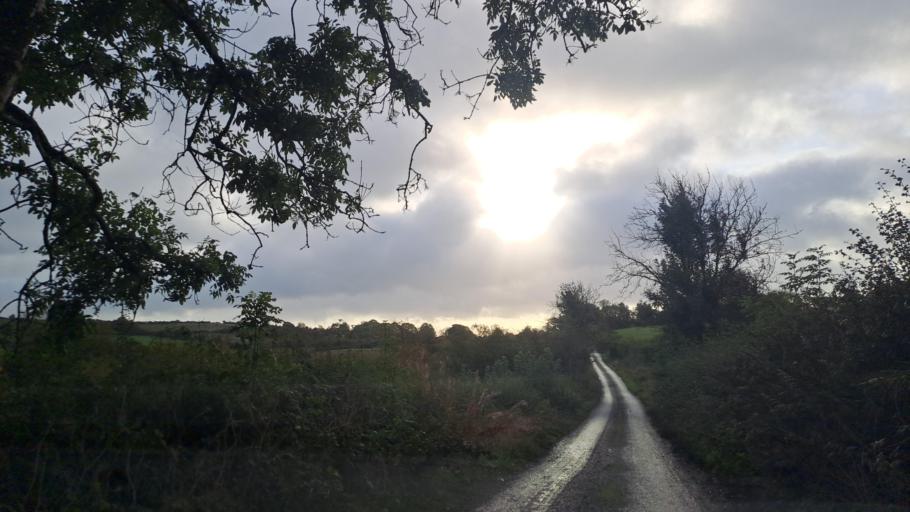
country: IE
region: Ulster
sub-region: An Cabhan
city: Kingscourt
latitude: 53.9636
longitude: -6.8262
